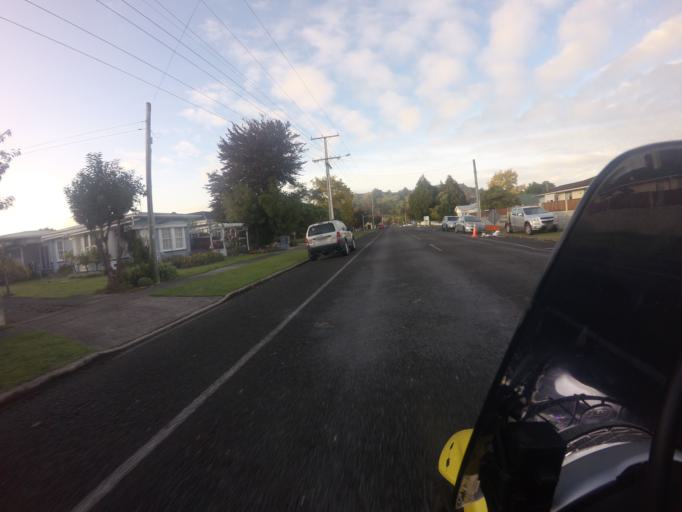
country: NZ
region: Gisborne
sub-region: Gisborne District
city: Gisborne
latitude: -38.6686
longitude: 178.0337
